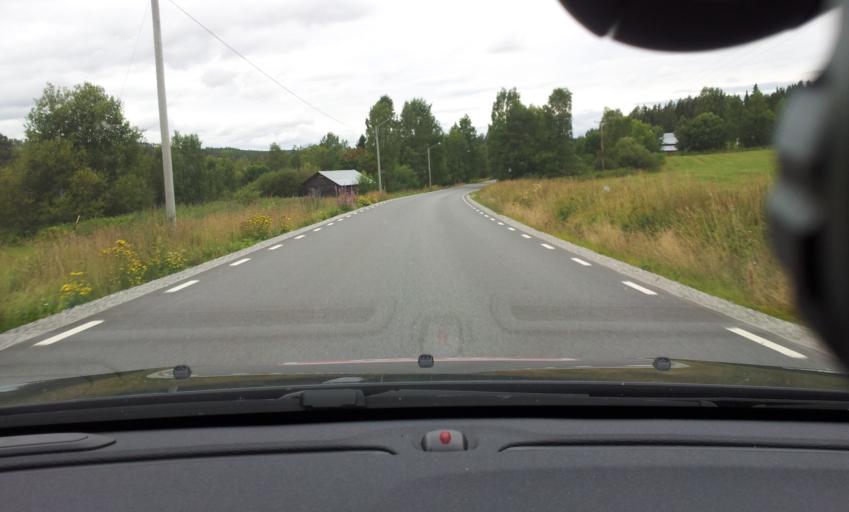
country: SE
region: Jaemtland
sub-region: Braecke Kommun
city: Braecke
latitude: 63.0778
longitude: 15.3933
